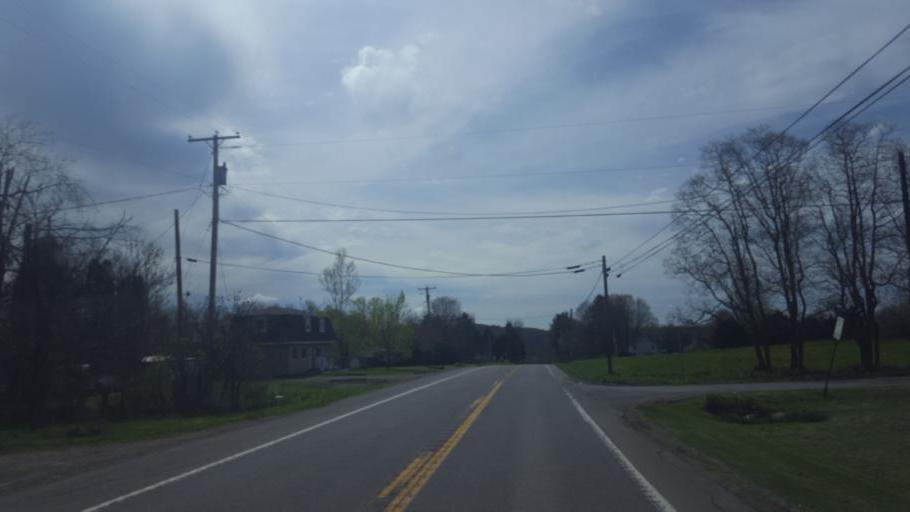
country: US
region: Pennsylvania
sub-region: Mercer County
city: Stoneboro
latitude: 41.3474
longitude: -80.0498
